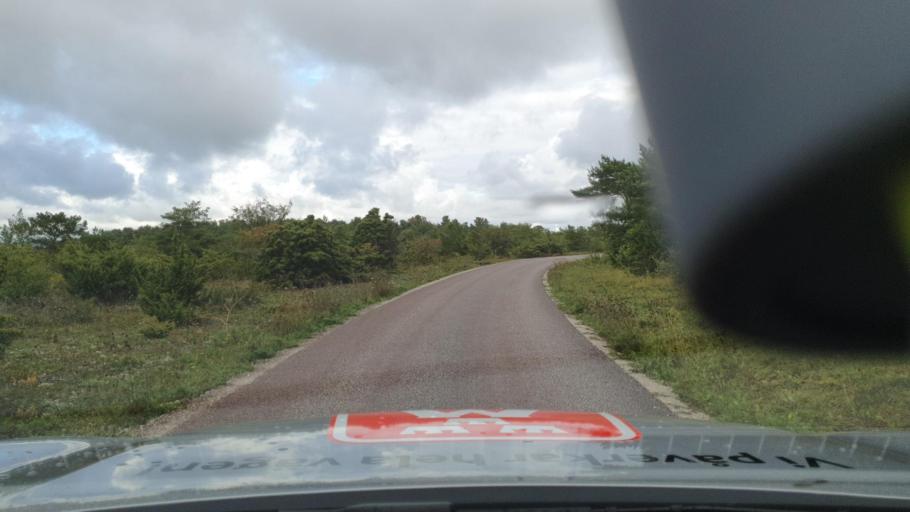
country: SE
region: Gotland
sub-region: Gotland
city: Hemse
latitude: 56.9806
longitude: 18.1971
